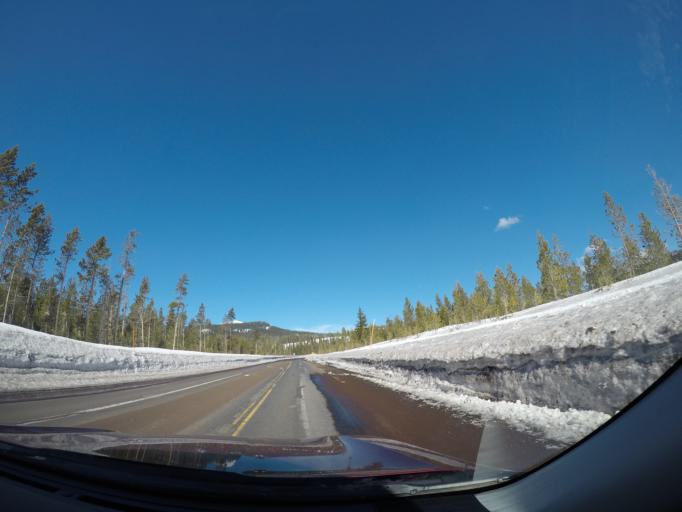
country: US
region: Oregon
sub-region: Deschutes County
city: Sunriver
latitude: 43.9792
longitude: -121.6121
